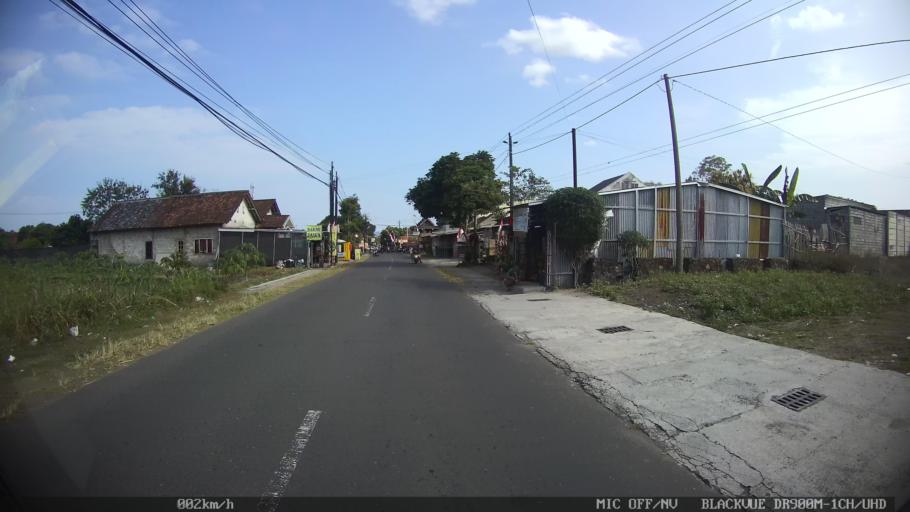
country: ID
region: Daerah Istimewa Yogyakarta
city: Depok
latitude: -7.7359
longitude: 110.4516
